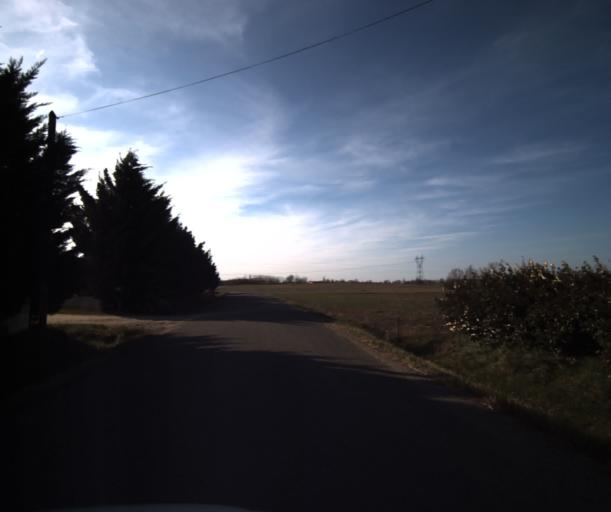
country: FR
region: Midi-Pyrenees
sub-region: Departement du Tarn-et-Garonne
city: Campsas
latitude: 43.9263
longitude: 1.3354
